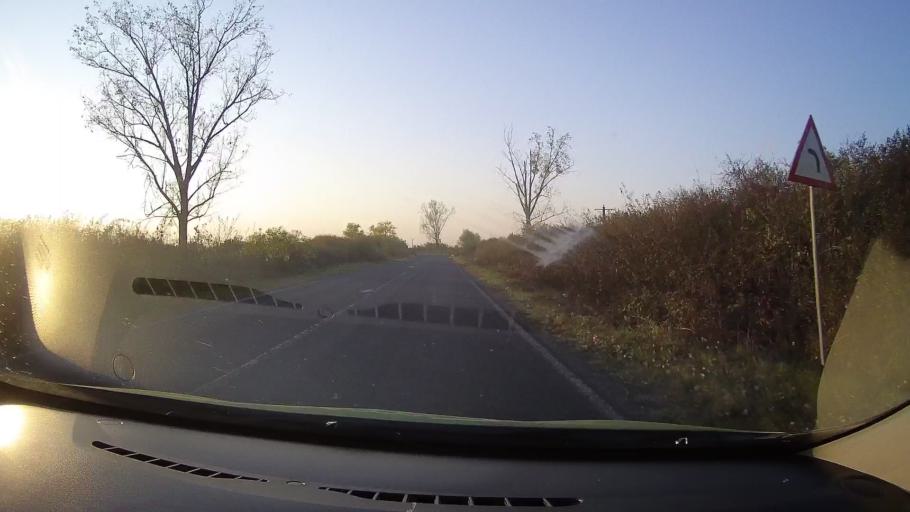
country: RO
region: Arad
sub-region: Comuna Bocsig
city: Bocsig
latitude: 46.4275
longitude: 21.9083
